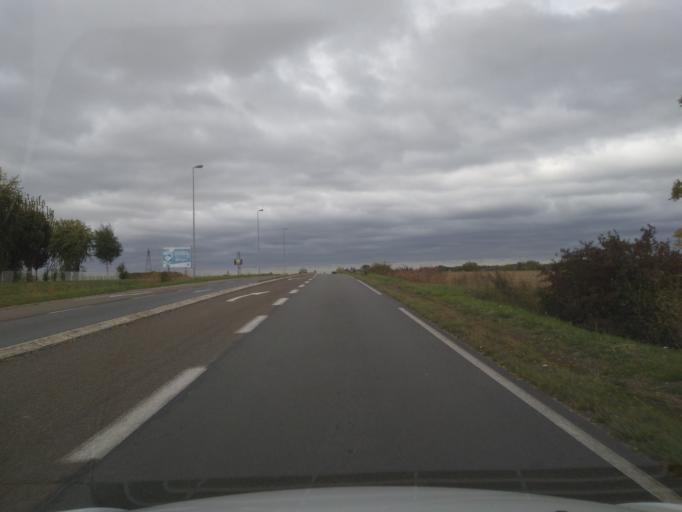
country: FR
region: Nord-Pas-de-Calais
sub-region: Departement du Nord
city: Marly
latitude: 50.3523
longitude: 3.5664
